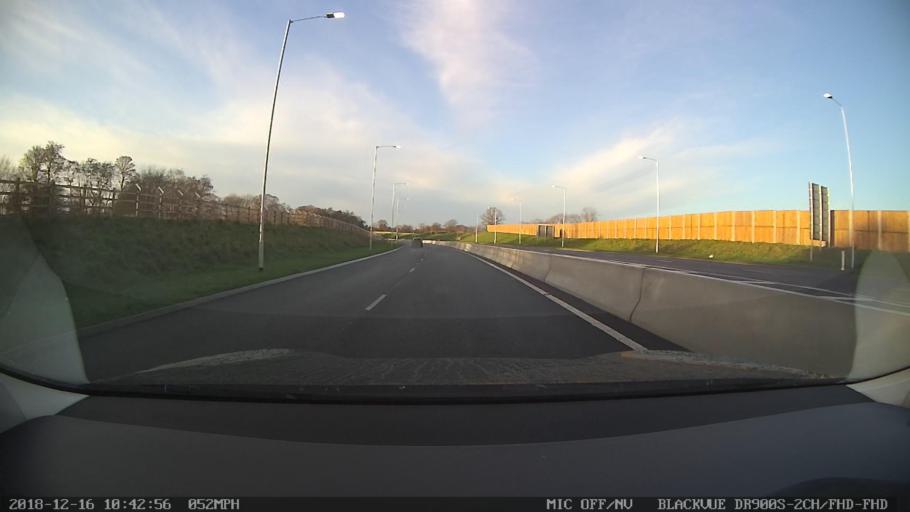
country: GB
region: England
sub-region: Cheshire East
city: Poynton
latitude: 53.3651
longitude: -2.1164
